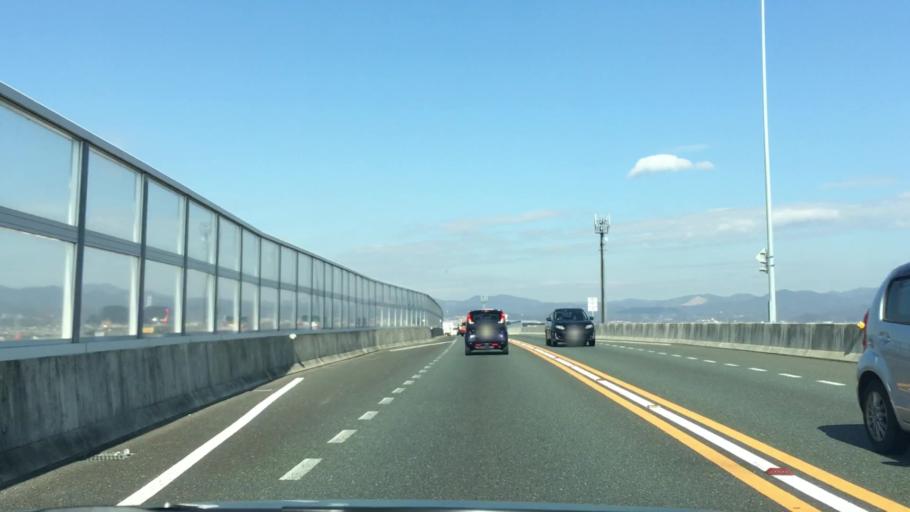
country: JP
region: Aichi
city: Kozakai-cho
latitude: 34.7851
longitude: 137.3329
